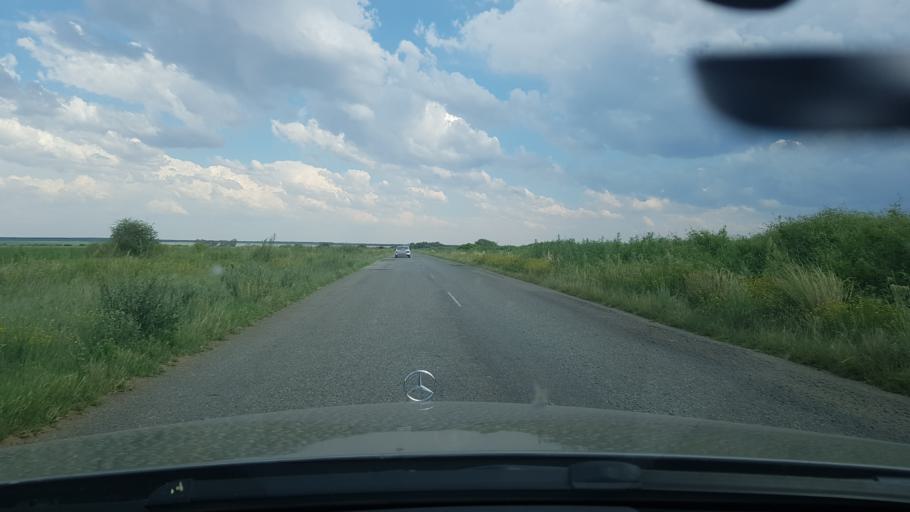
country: ZA
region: North-West
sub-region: Dr Ruth Segomotsi Mompati District Municipality
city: Bloemhof
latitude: -27.8371
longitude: 25.6400
